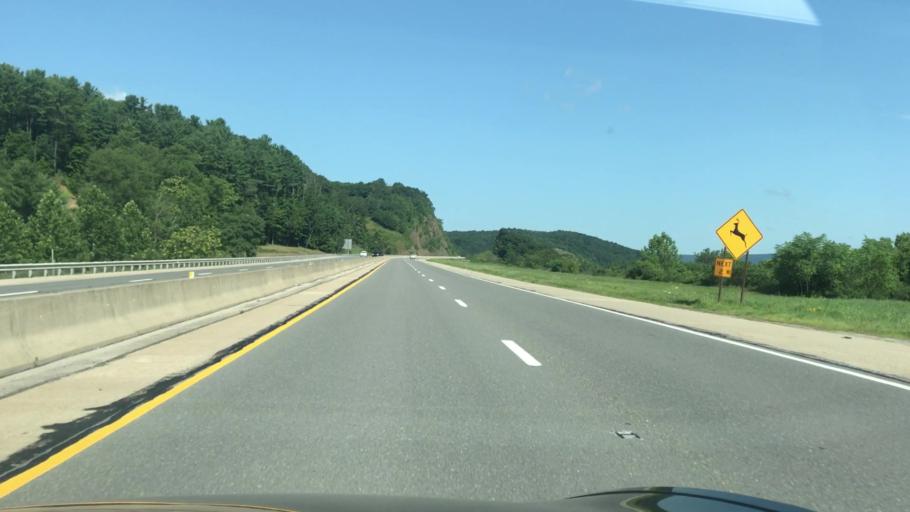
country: US
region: Pennsylvania
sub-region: Lycoming County
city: Garden View
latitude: 41.2677
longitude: -77.0518
